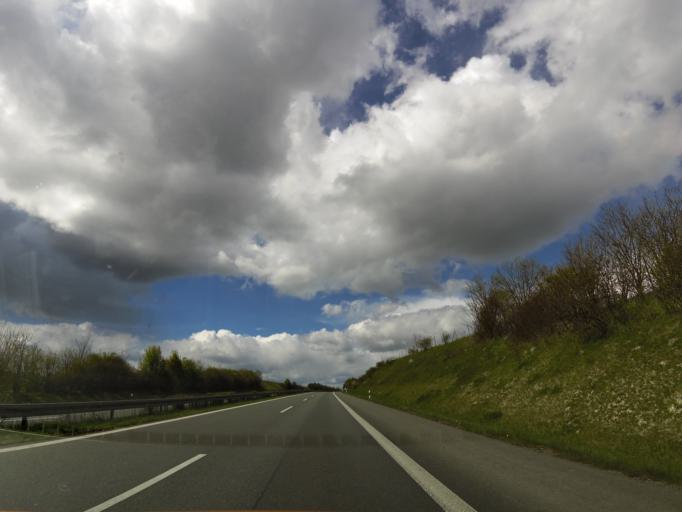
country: DE
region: Saxony-Anhalt
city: Stapelburg
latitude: 51.9011
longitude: 10.6902
